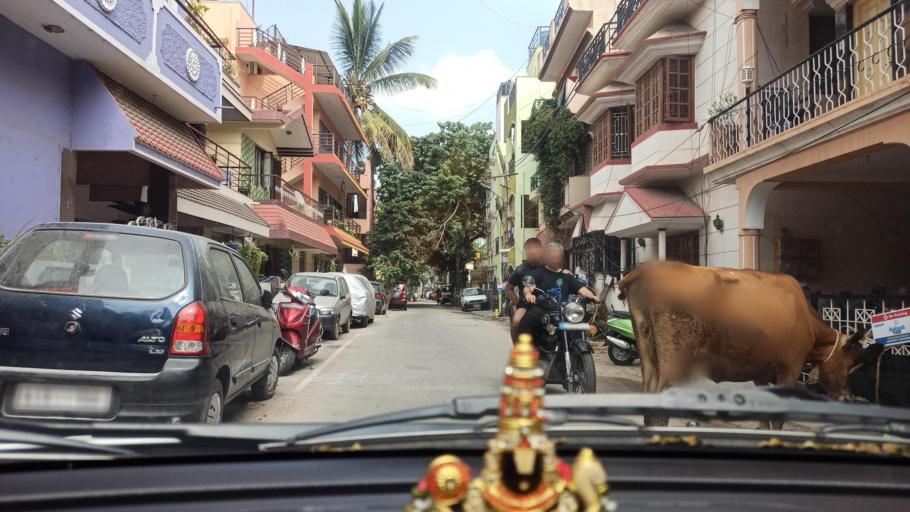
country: IN
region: Karnataka
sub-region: Bangalore Urban
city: Bangalore
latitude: 13.0122
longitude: 77.6699
